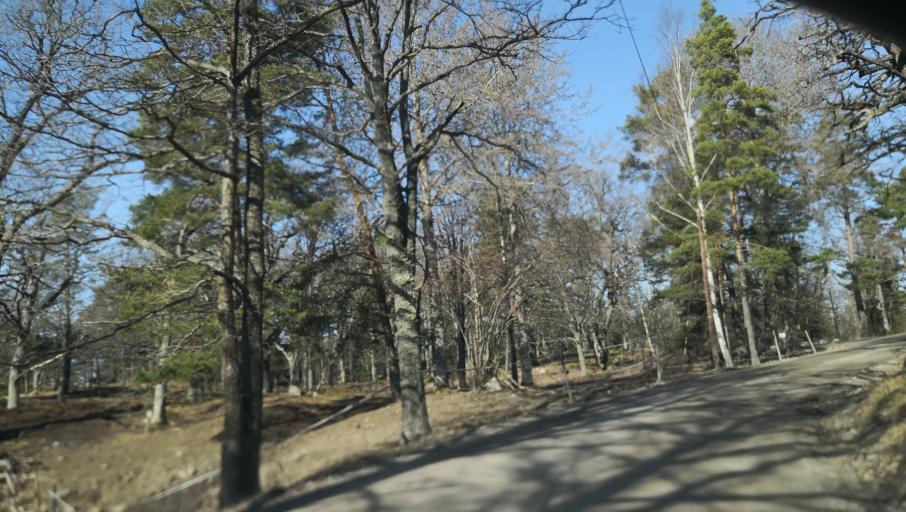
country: SE
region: Stockholm
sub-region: Varmdo Kommun
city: Gustavsberg
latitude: 59.2982
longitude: 18.3549
